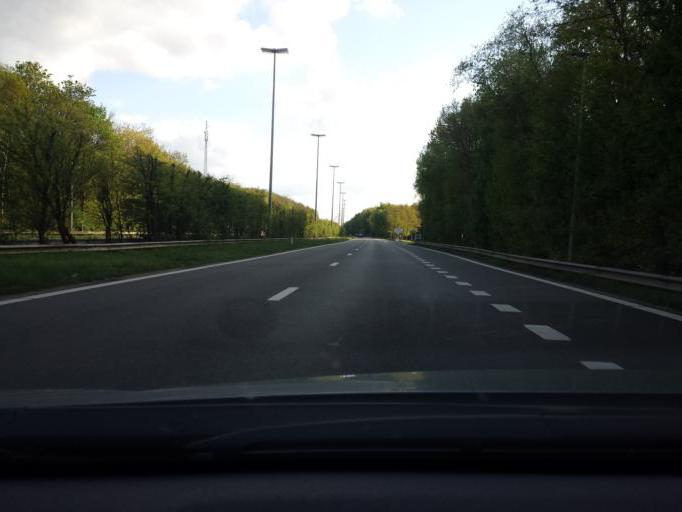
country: BE
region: Wallonia
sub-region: Province de Liege
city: Lontzen
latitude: 50.6894
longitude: 6.0589
